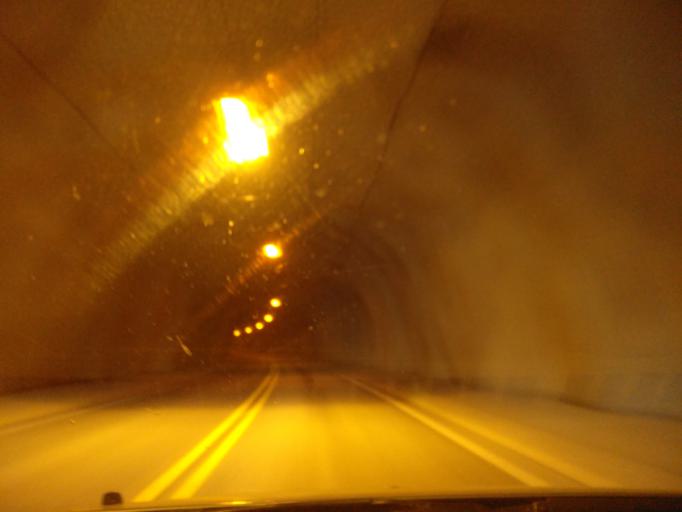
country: NO
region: Rogaland
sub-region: Sauda
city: Sauda
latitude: 59.8272
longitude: 6.2454
